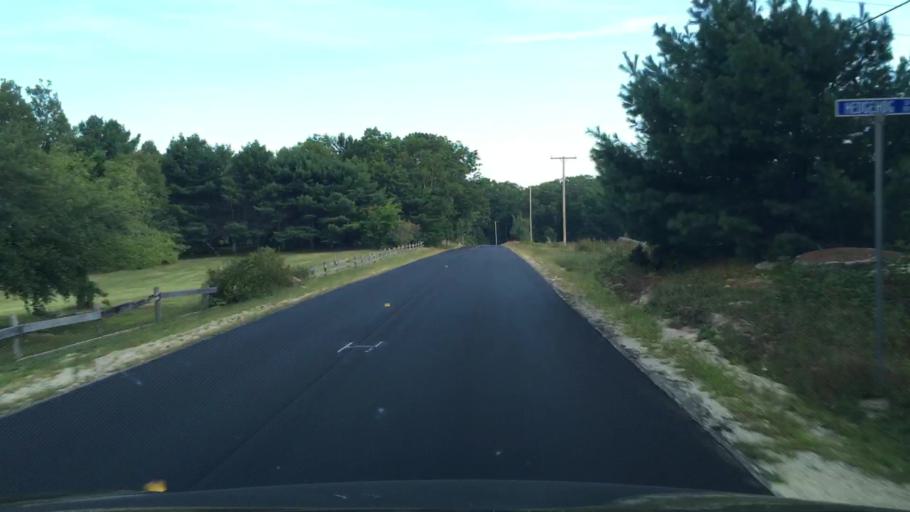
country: US
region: Maine
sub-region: Hancock County
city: Surry
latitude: 44.5277
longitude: -68.6109
